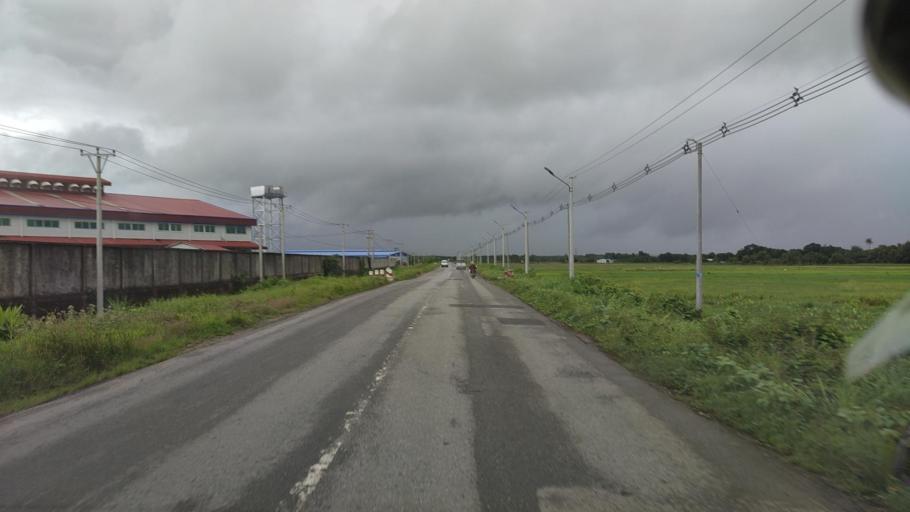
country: MM
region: Bago
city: Bago
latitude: 17.3753
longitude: 96.4726
